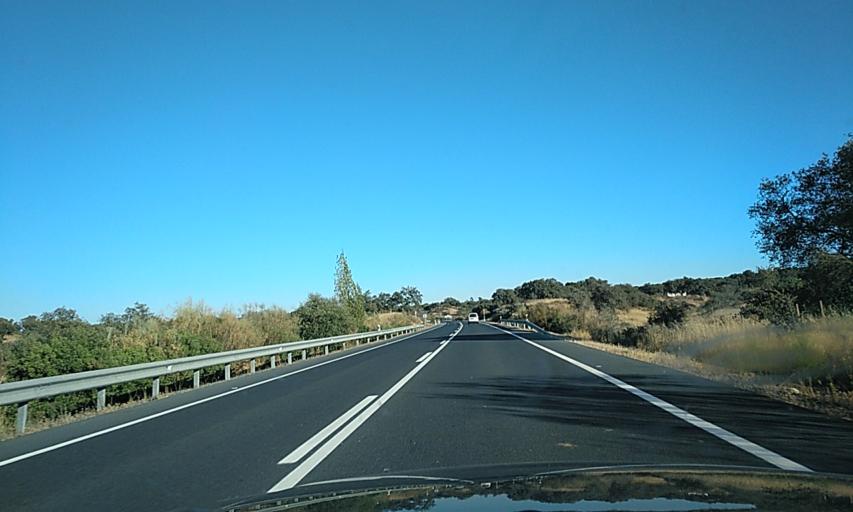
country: ES
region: Andalusia
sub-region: Provincia de Huelva
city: San Bartolome de la Torre
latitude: 37.4402
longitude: -7.1194
